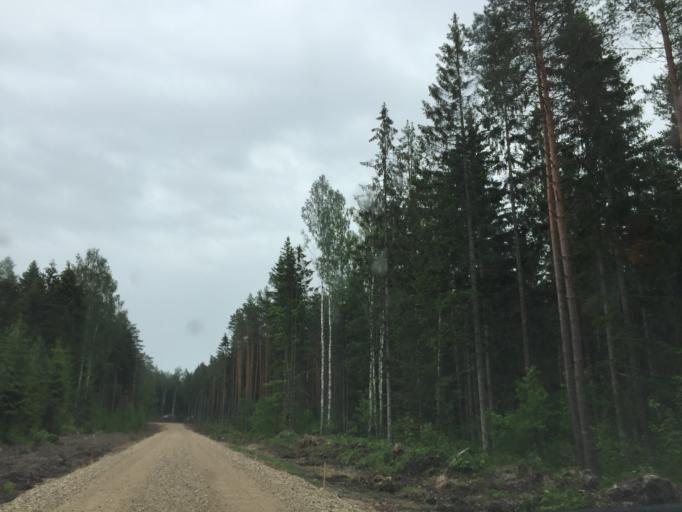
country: LV
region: Tukuma Rajons
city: Tukums
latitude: 57.0046
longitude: 23.1064
